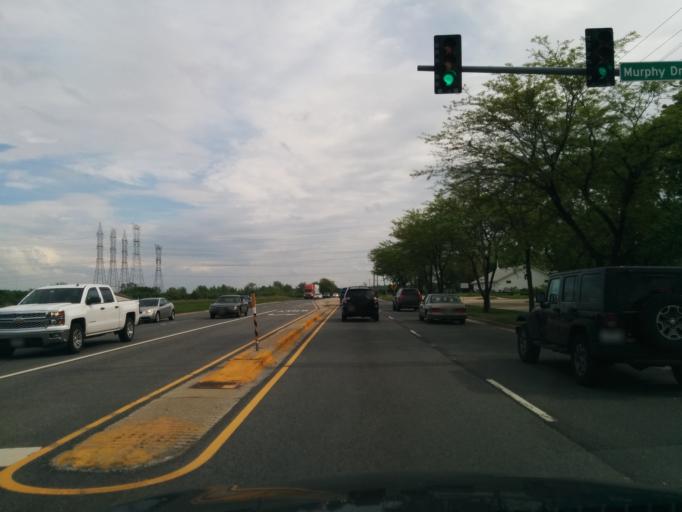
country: US
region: Illinois
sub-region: Will County
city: Romeoville
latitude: 41.6351
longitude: -88.0805
